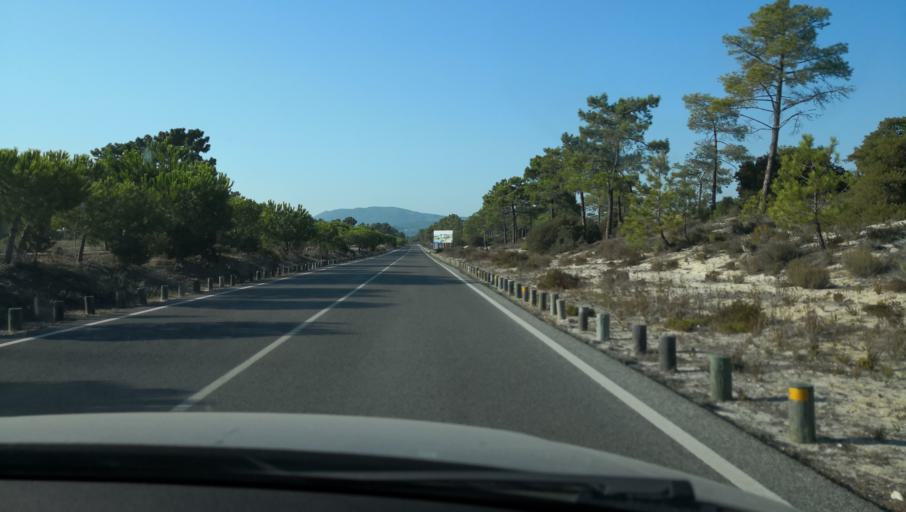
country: PT
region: Setubal
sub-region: Setubal
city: Setubal
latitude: 38.4777
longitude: -8.8881
